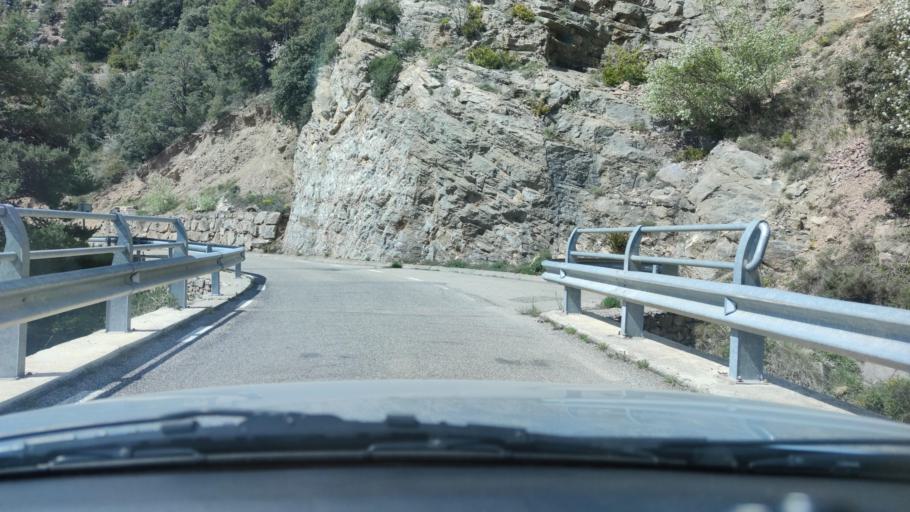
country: ES
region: Catalonia
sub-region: Provincia de Lleida
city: Coll de Nargo
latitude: 42.2939
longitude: 1.2651
